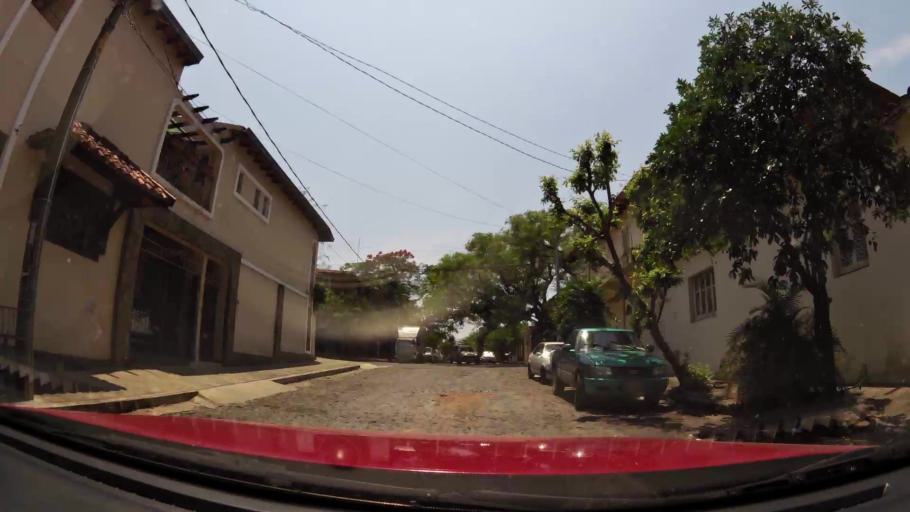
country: PY
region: Asuncion
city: Asuncion
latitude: -25.2935
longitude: -57.6465
